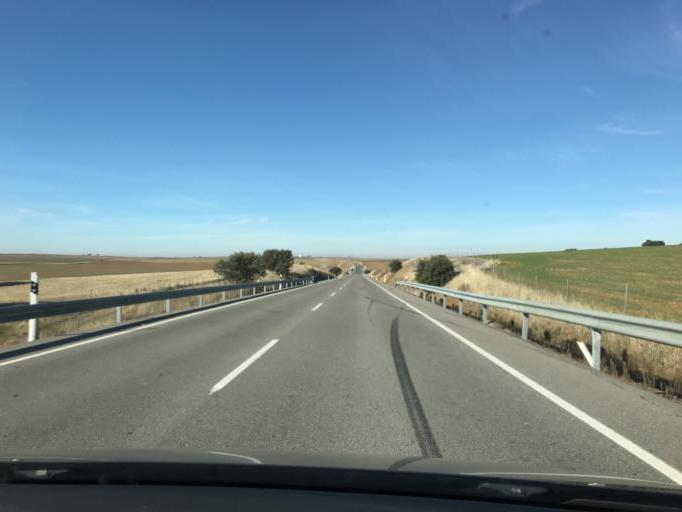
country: ES
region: Extremadura
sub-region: Provincia de Badajoz
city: Granja de Torrehermosa
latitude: 38.2926
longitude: -5.5388
